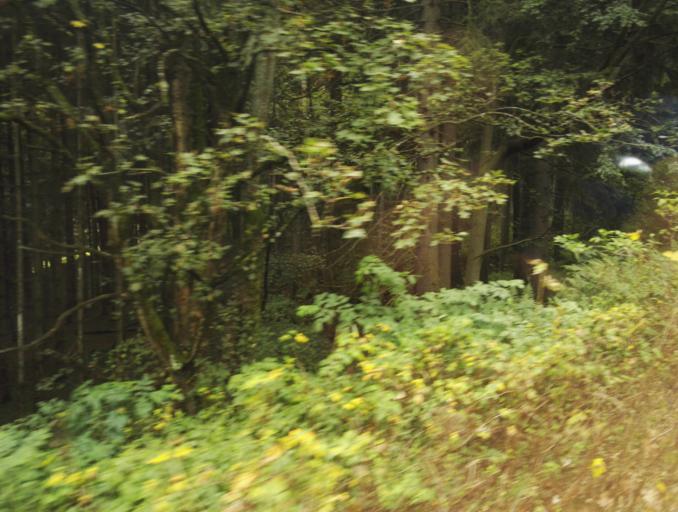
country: AT
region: Styria
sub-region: Politischer Bezirk Leoben
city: Vordernberg
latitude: 47.5105
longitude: 14.9818
